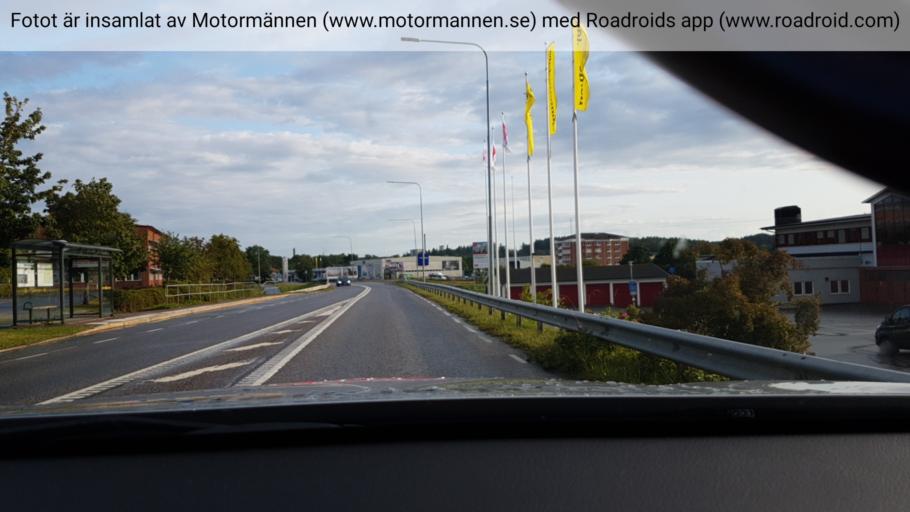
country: SE
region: Stockholm
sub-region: Norrtalje Kommun
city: Norrtalje
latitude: 59.7628
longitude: 18.6904
